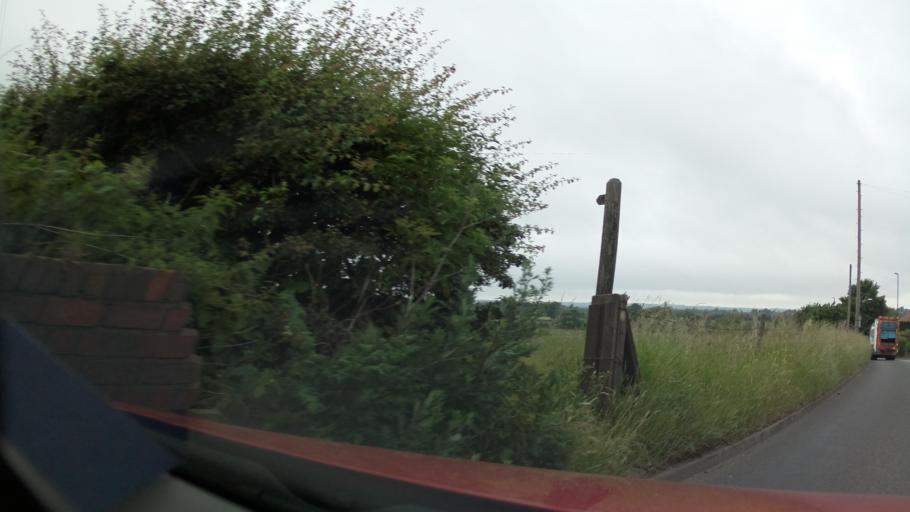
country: GB
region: England
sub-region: Derbyshire
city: Swadlincote
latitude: 52.7762
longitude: -1.6023
